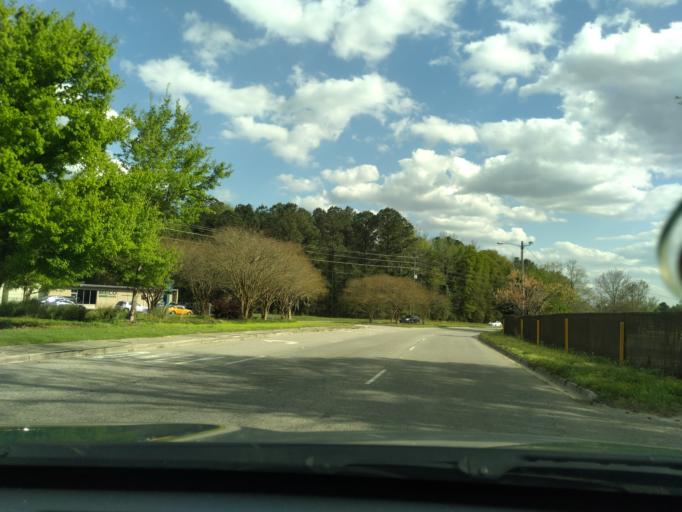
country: US
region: South Carolina
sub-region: Florence County
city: Florence
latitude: 34.1817
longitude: -79.7619
